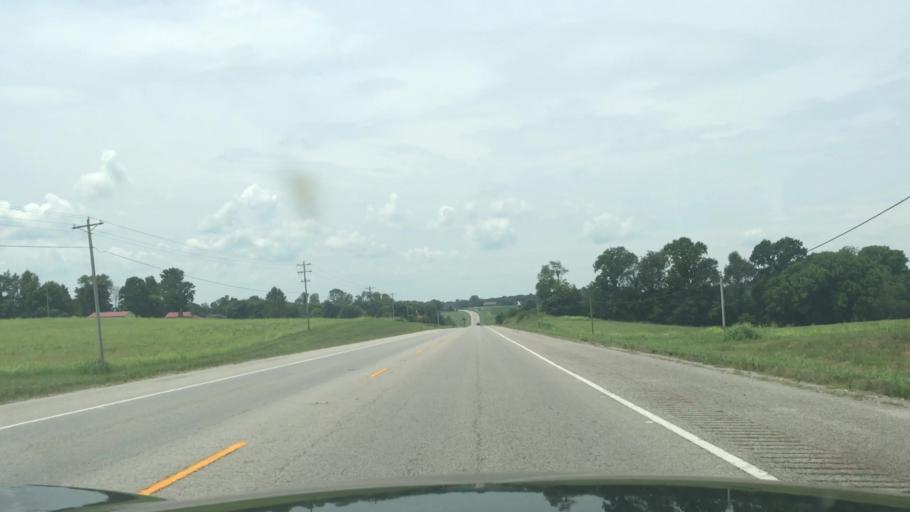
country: US
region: Kentucky
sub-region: Green County
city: Greensburg
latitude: 37.2983
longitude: -85.4558
